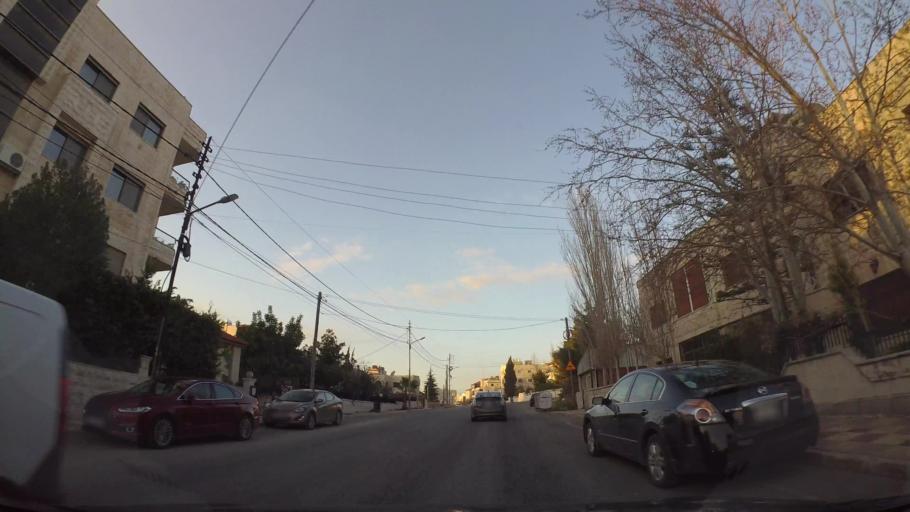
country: JO
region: Amman
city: Al Jubayhah
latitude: 31.9941
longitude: 35.8744
